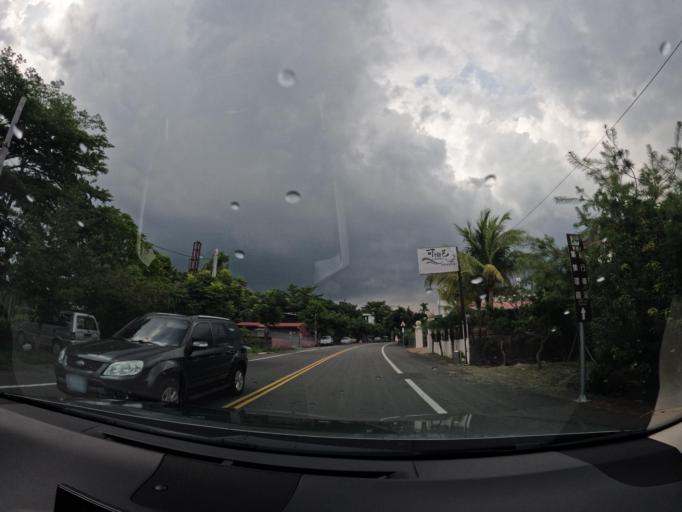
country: TW
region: Taiwan
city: Lugu
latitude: 23.8254
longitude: 120.7926
